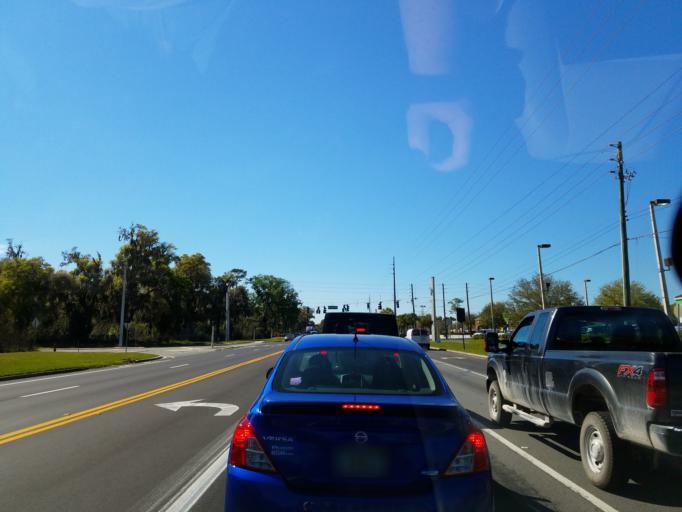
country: US
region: Florida
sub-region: Marion County
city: Ocala
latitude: 29.2104
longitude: -82.1931
